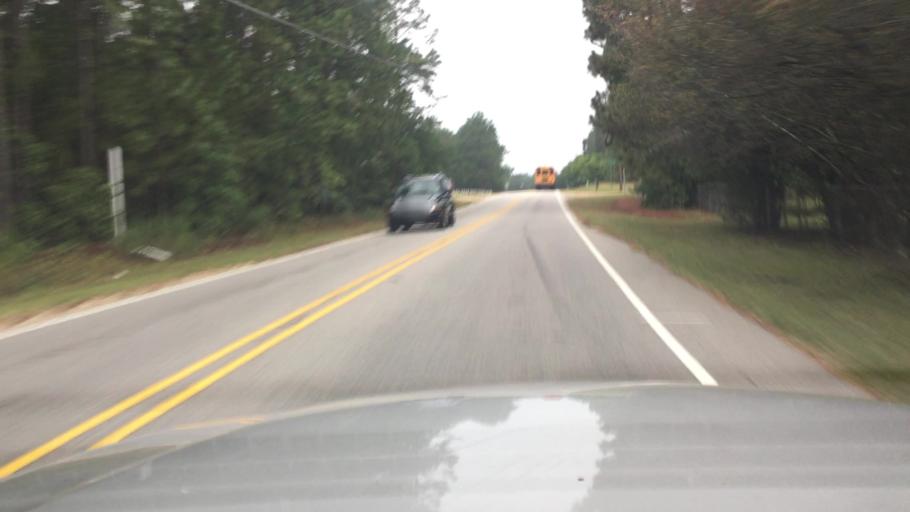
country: US
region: North Carolina
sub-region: Cumberland County
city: Hope Mills
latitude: 34.9731
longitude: -78.9643
